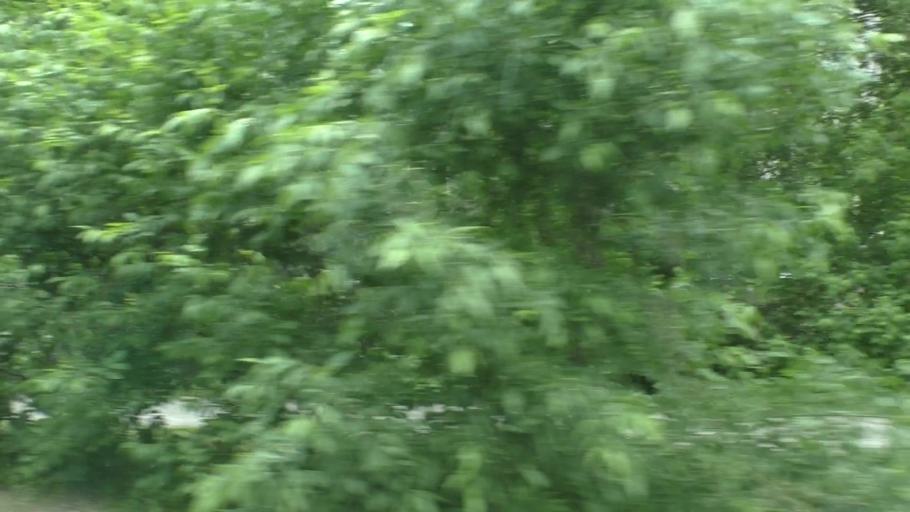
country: RU
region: Moskovskaya
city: Yegor'yevsk
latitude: 55.3682
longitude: 39.0547
